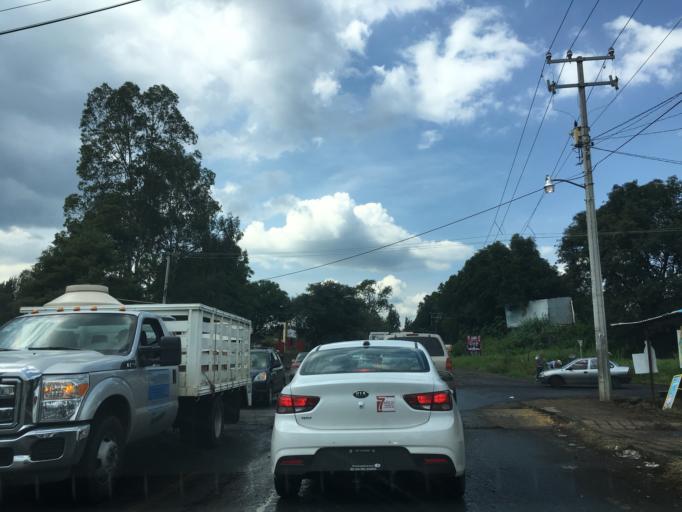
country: MX
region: Michoacan
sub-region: Tingueindin
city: Tingueindin
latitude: 19.7430
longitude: -102.4845
